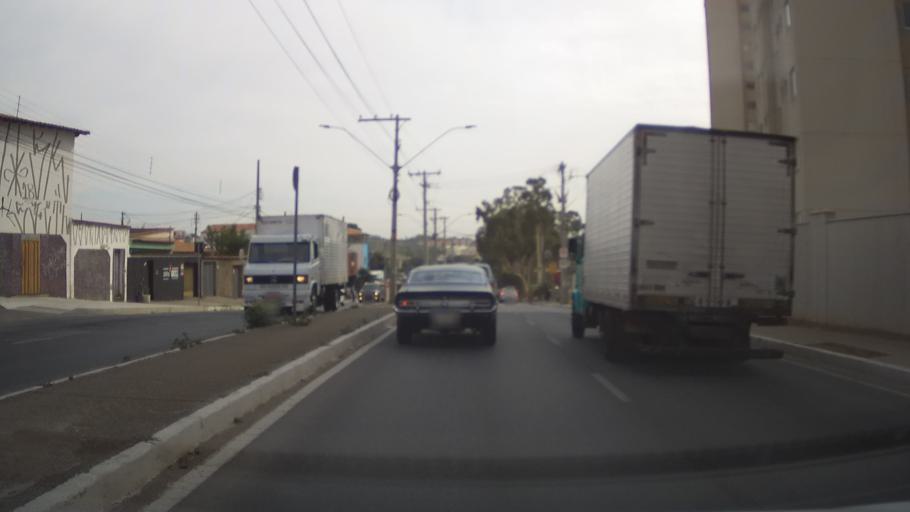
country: BR
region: Minas Gerais
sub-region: Contagem
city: Contagem
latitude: -19.9449
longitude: -44.0282
